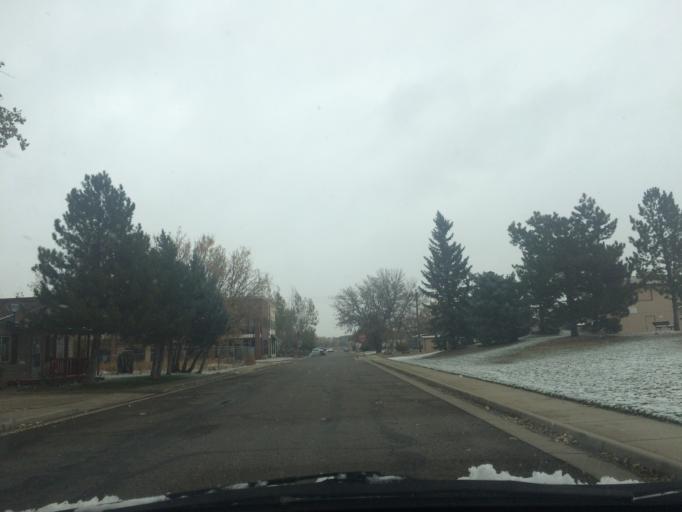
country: US
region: Colorado
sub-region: Boulder County
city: Erie
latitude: 40.0492
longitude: -105.0468
